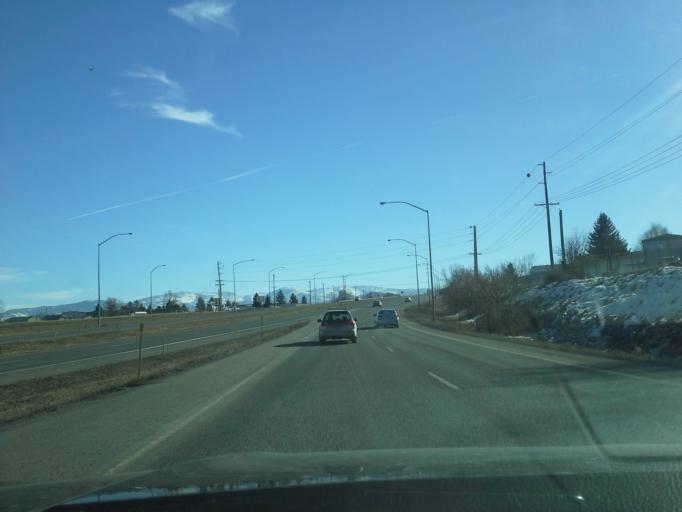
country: US
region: Montana
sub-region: Lewis and Clark County
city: Helena
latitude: 46.6054
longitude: -112.0077
